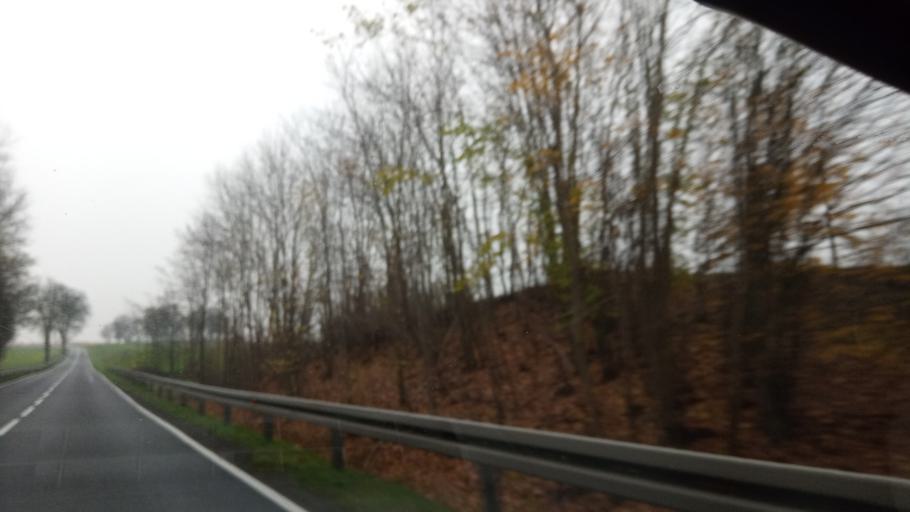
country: PL
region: Kujawsko-Pomorskie
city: Kamien Krajenski
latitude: 53.5567
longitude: 17.5021
